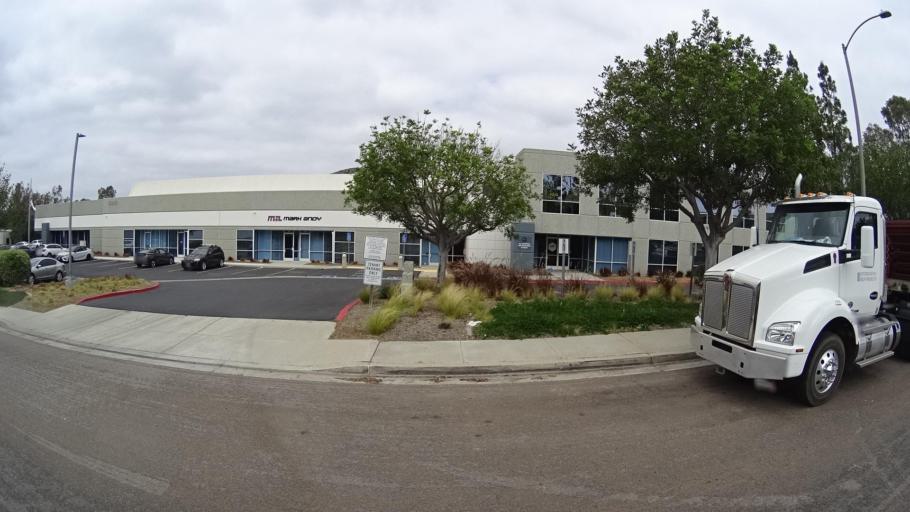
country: US
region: California
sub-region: San Diego County
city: Poway
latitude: 33.0170
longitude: -117.1007
